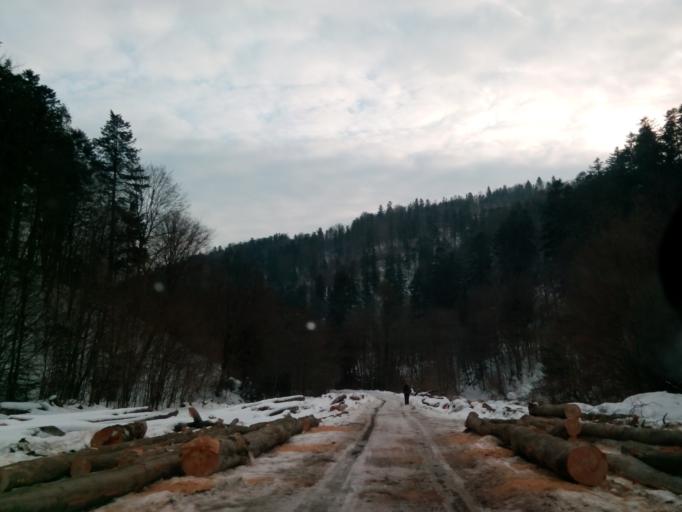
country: SK
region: Presovsky
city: Sabinov
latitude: 49.2031
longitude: 21.0831
